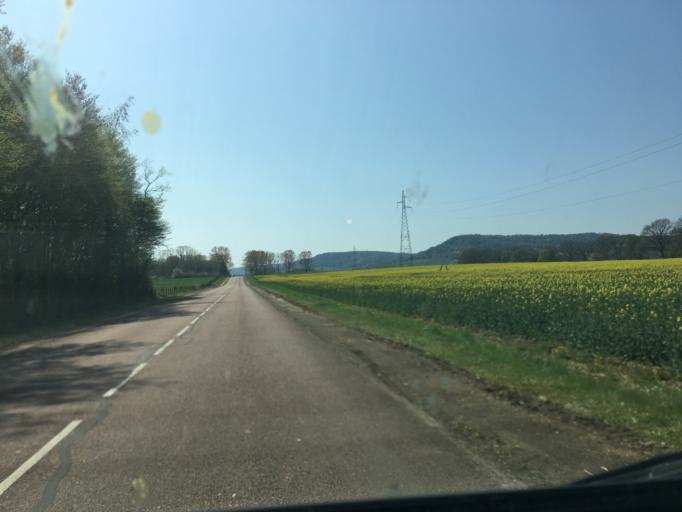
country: FR
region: Lorraine
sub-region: Departement de la Meuse
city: Vigneulles-les-Hattonchatel
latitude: 48.9474
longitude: 5.7243
